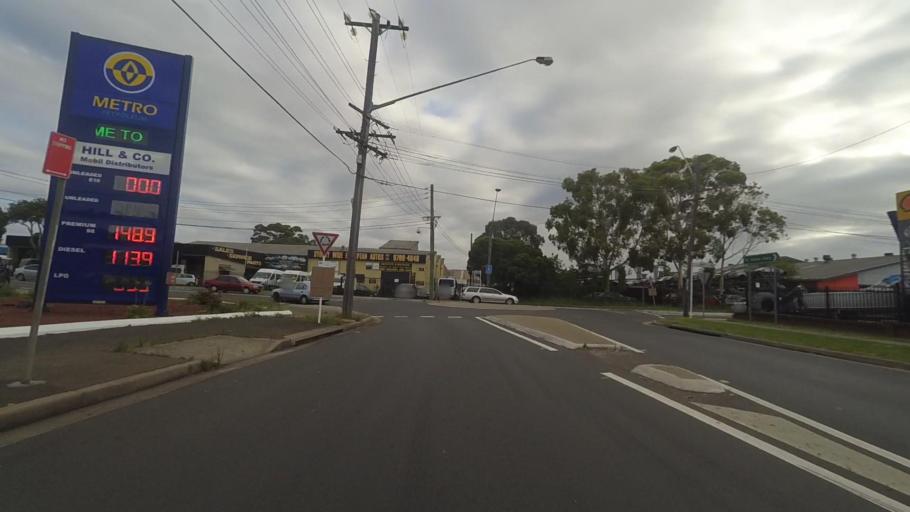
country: AU
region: New South Wales
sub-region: Bankstown
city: Revesby
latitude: -33.9307
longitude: 151.0118
